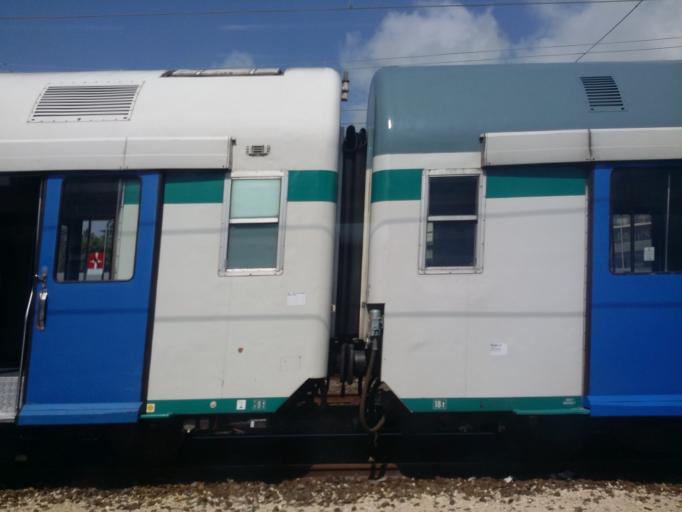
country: IT
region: Liguria
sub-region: Provincia di Savona
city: Savona
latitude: 44.3048
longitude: 8.4699
